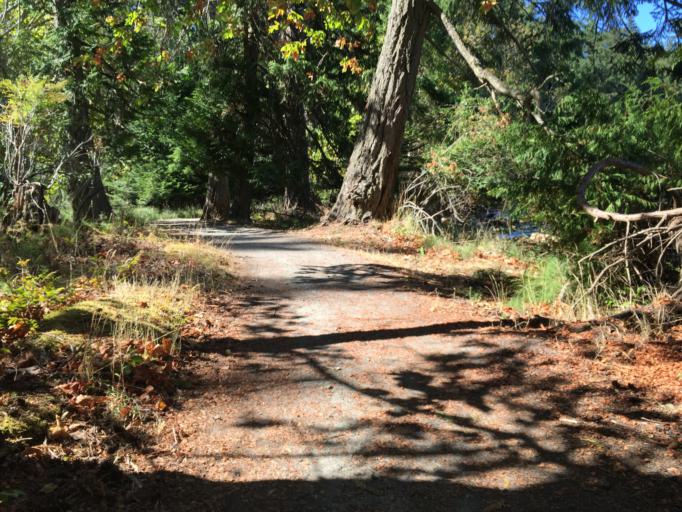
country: CA
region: British Columbia
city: Nanaimo
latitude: 49.1935
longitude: -123.9271
